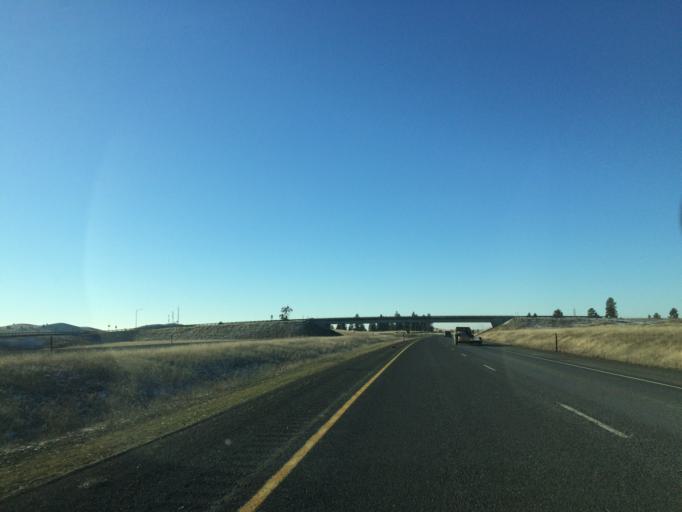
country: US
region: Washington
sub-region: Spokane County
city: Medical Lake
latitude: 47.3975
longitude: -117.8387
